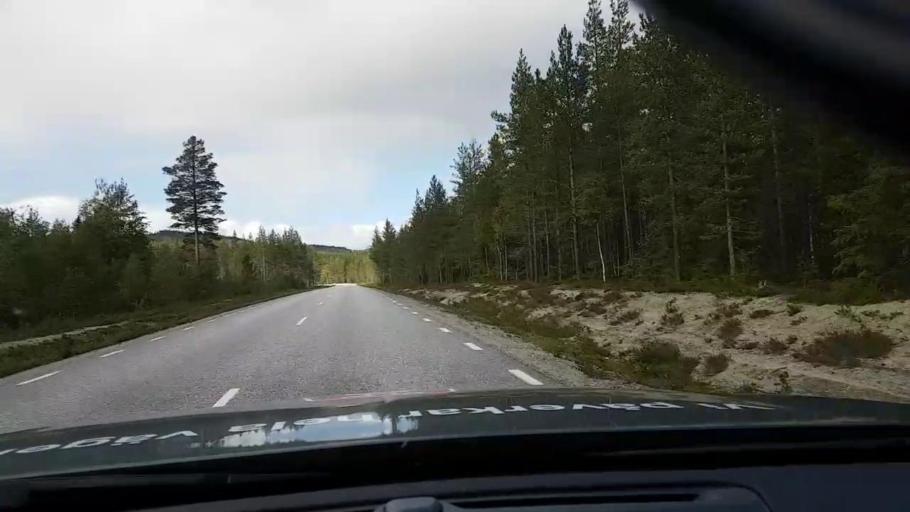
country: SE
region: Vaesternorrland
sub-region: OErnskoeldsviks Kommun
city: Bredbyn
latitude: 63.6825
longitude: 17.7812
